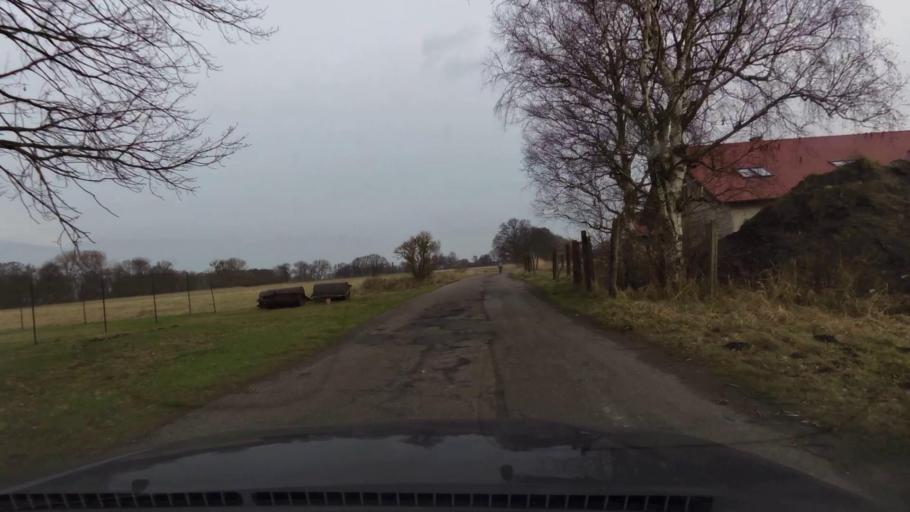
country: PL
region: West Pomeranian Voivodeship
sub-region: Powiat goleniowski
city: Stepnica
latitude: 53.7236
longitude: 14.5545
